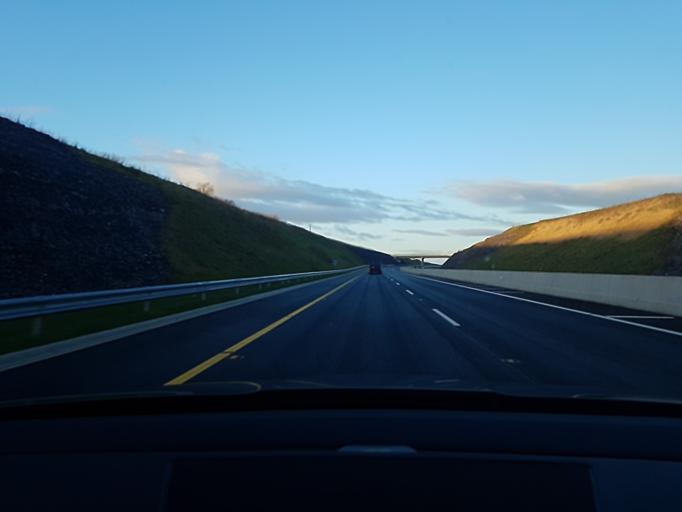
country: IE
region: Connaught
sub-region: County Galway
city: Athenry
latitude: 53.3449
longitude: -8.8016
